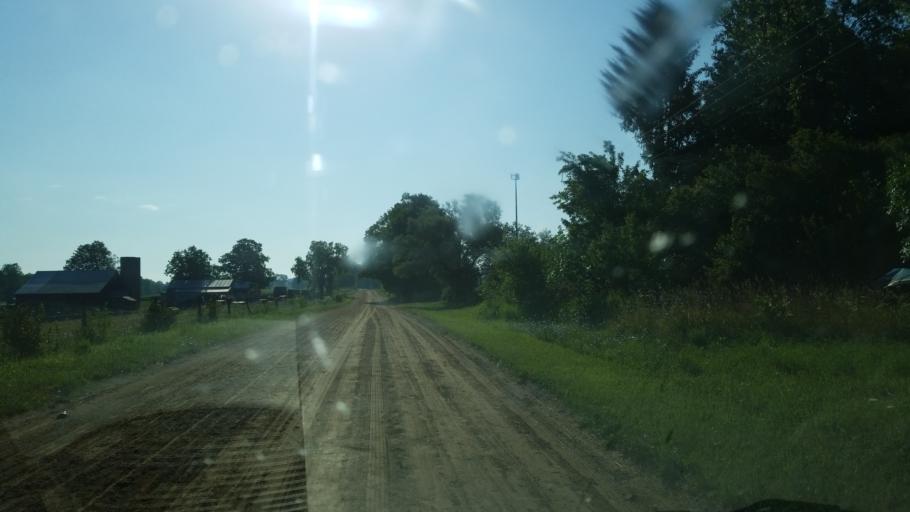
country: US
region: Michigan
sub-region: Mecosta County
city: Canadian Lakes
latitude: 43.5690
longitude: -85.3670
